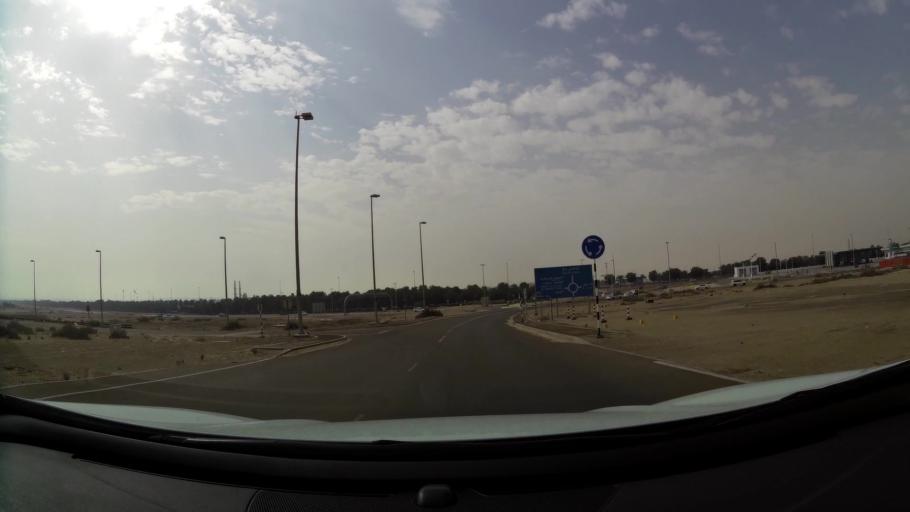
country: AE
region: Abu Dhabi
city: Abu Dhabi
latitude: 24.2723
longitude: 54.6661
